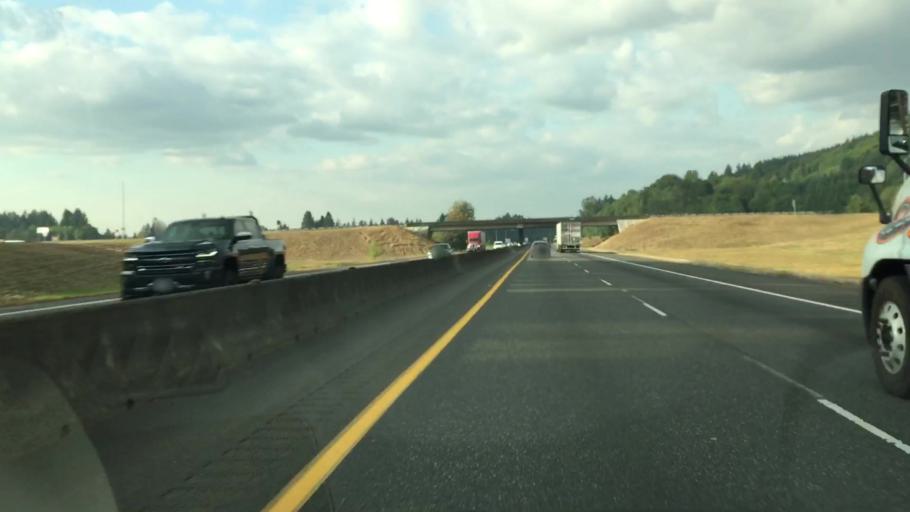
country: US
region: Washington
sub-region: Lewis County
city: Winlock
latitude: 46.3890
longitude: -122.9012
